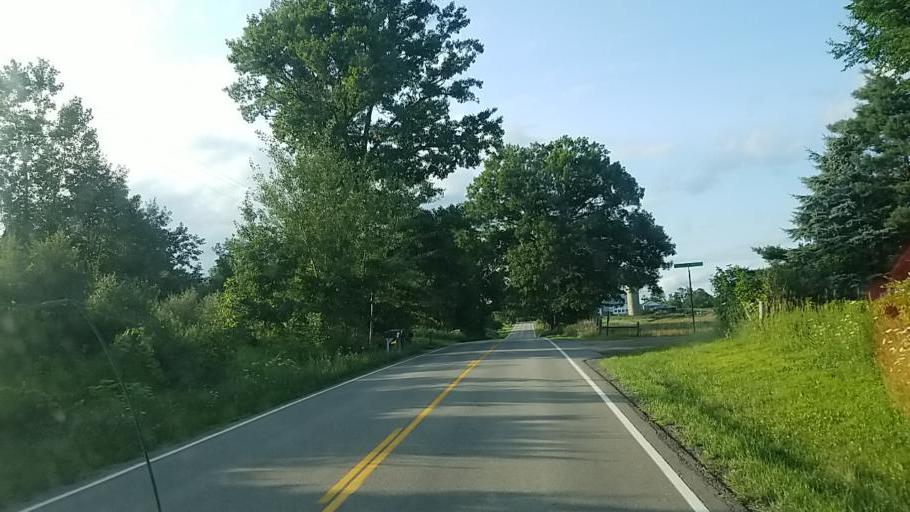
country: US
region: Michigan
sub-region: Montcalm County
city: Greenville
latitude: 43.2567
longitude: -85.3721
